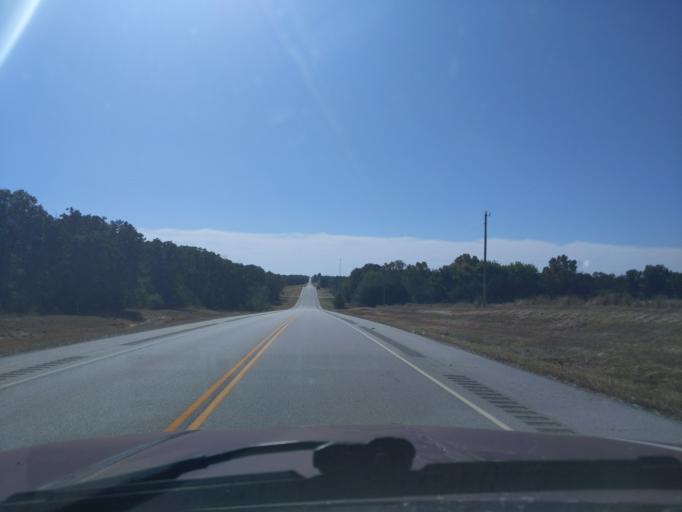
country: US
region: Oklahoma
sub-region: Creek County
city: Bristow
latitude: 35.7442
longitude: -96.3872
